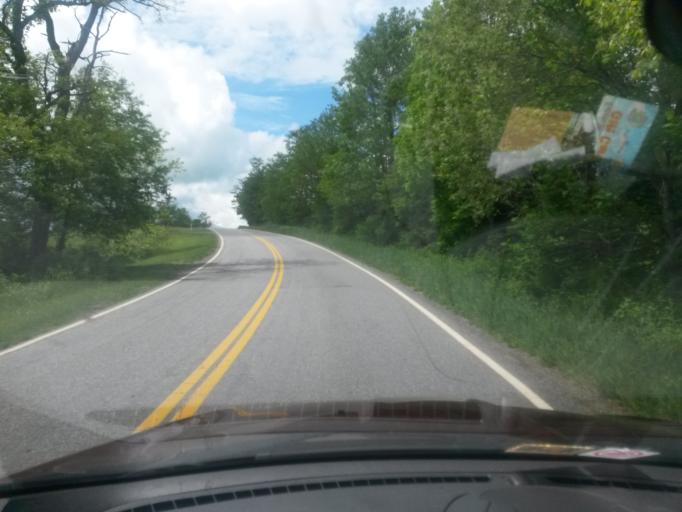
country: US
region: Virginia
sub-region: Patrick County
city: Stuart
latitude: 36.7466
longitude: -80.3904
